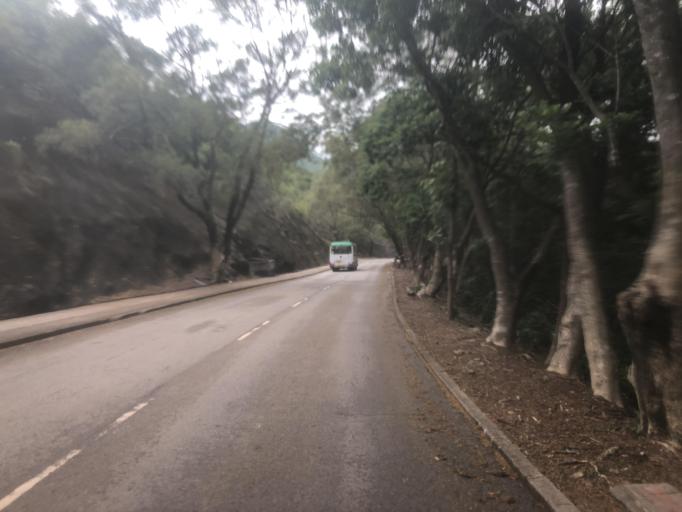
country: HK
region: Sai Kung
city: Sai Kung
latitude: 22.3961
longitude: 114.3277
